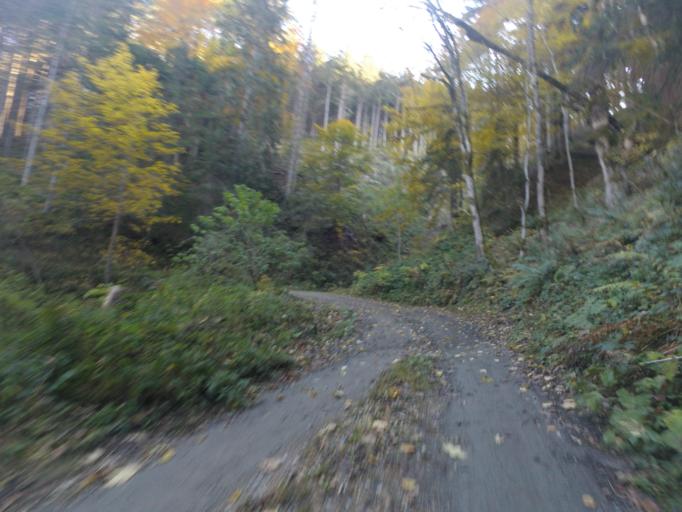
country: AT
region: Salzburg
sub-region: Politischer Bezirk Sankt Johann im Pongau
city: Sankt Johann im Pongau
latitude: 47.3268
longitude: 13.2219
